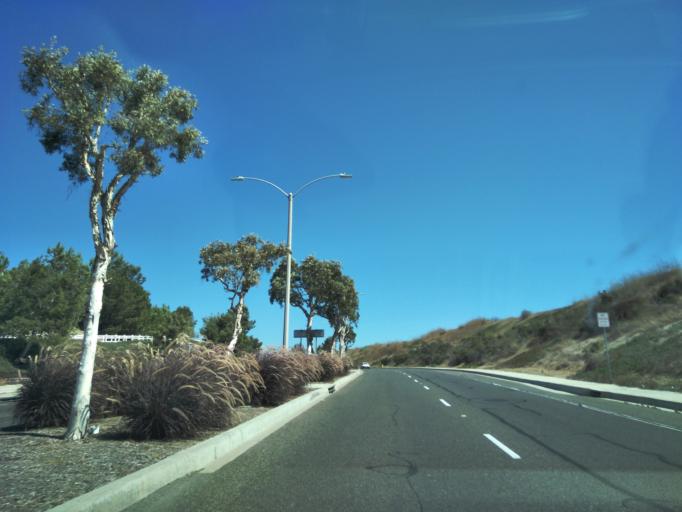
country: US
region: California
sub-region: Orange County
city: San Clemente
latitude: 33.4563
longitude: -117.6161
